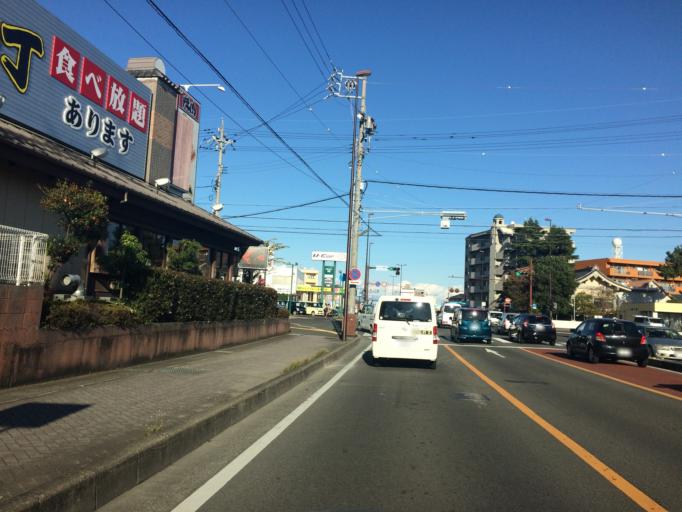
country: JP
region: Shizuoka
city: Shizuoka-shi
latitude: 34.9546
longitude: 138.3822
